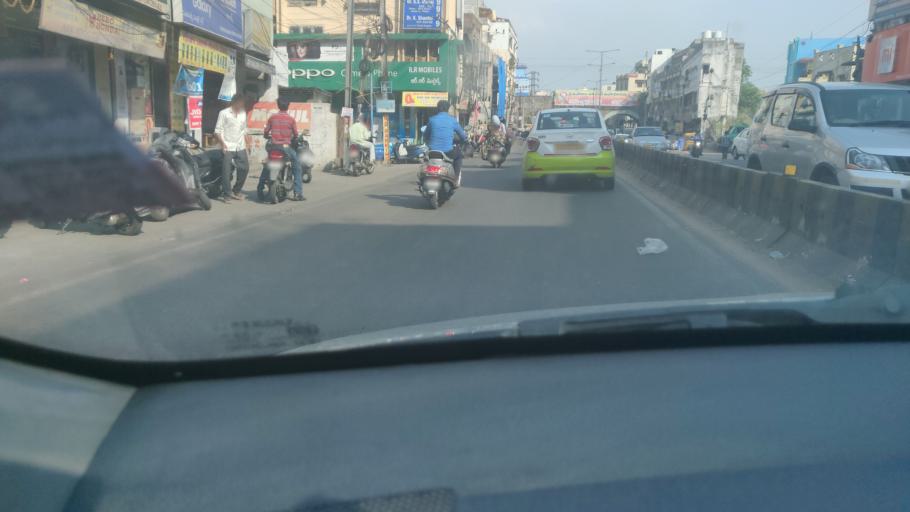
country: IN
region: Telangana
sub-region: Rangareddi
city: Gaddi Annaram
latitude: 17.3958
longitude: 78.5035
